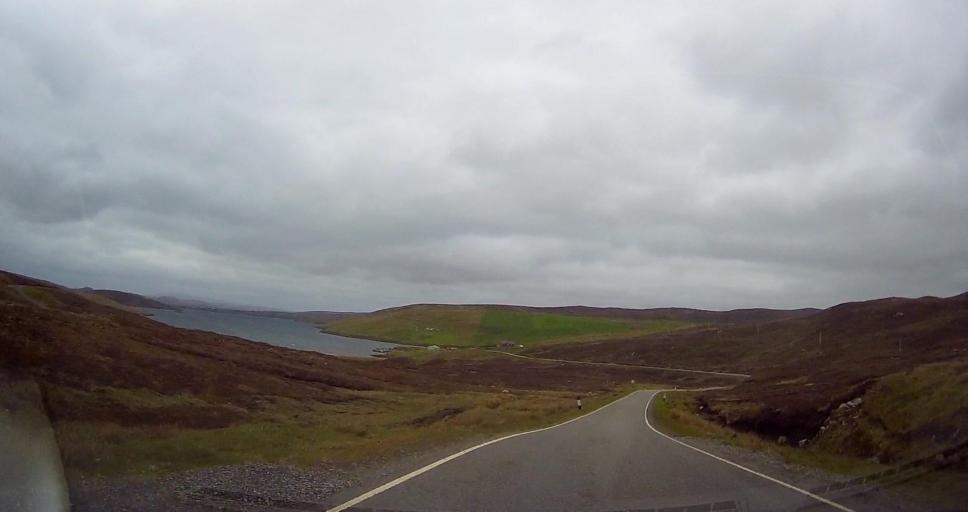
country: GB
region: Scotland
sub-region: Shetland Islands
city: Lerwick
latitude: 60.3284
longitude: -1.3383
